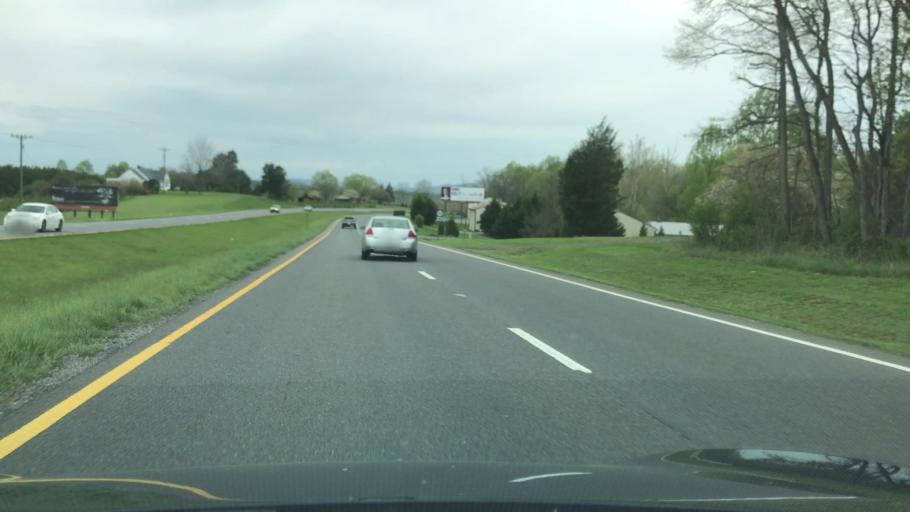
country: US
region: Virginia
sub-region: Bedford County
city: Forest
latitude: 37.3017
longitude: -79.3807
